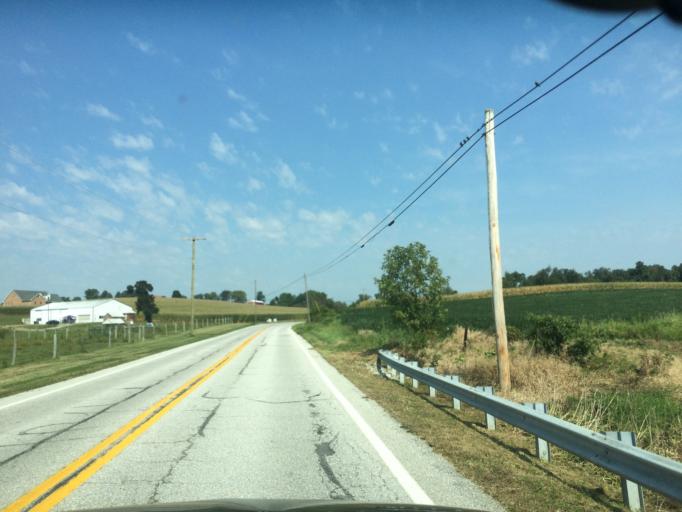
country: US
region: Maryland
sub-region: Carroll County
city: New Windsor
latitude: 39.5618
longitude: -77.1225
